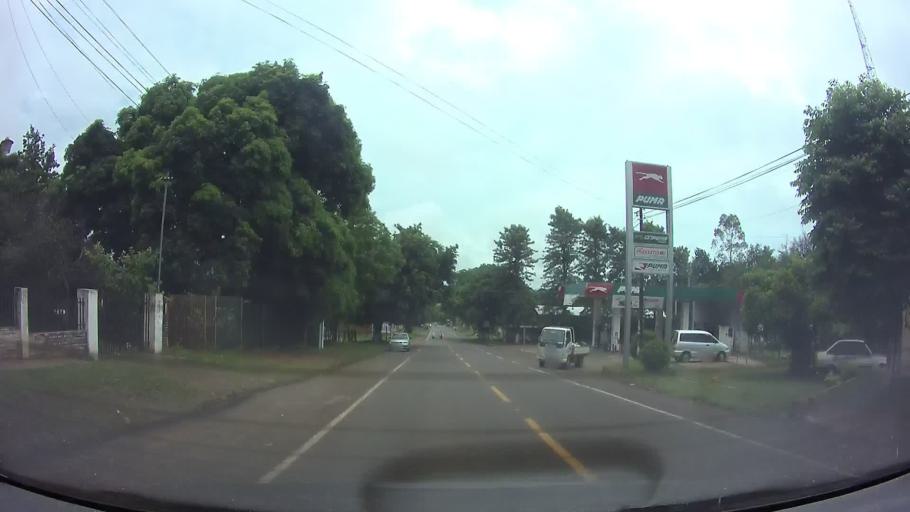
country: PY
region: Paraguari
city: Acahay
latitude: -25.9100
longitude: -57.1147
